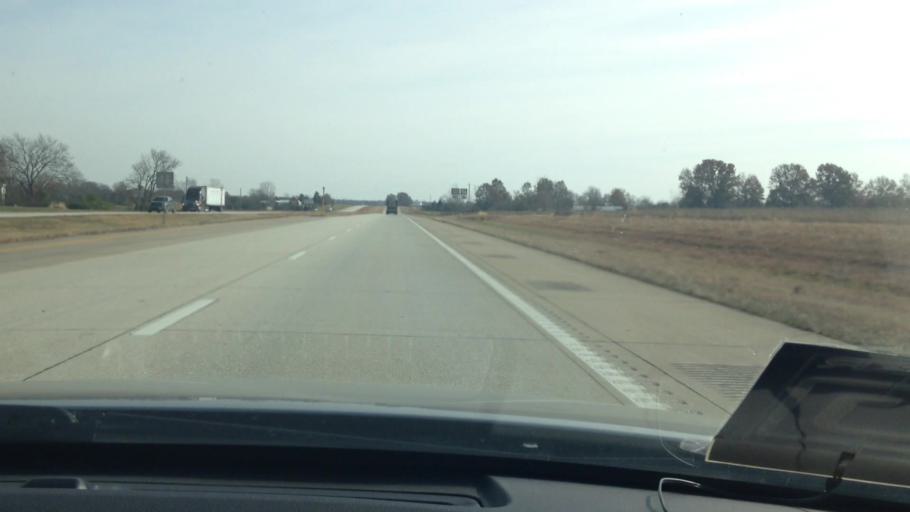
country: US
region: Missouri
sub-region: Henry County
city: Clinton
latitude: 38.4346
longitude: -93.9350
